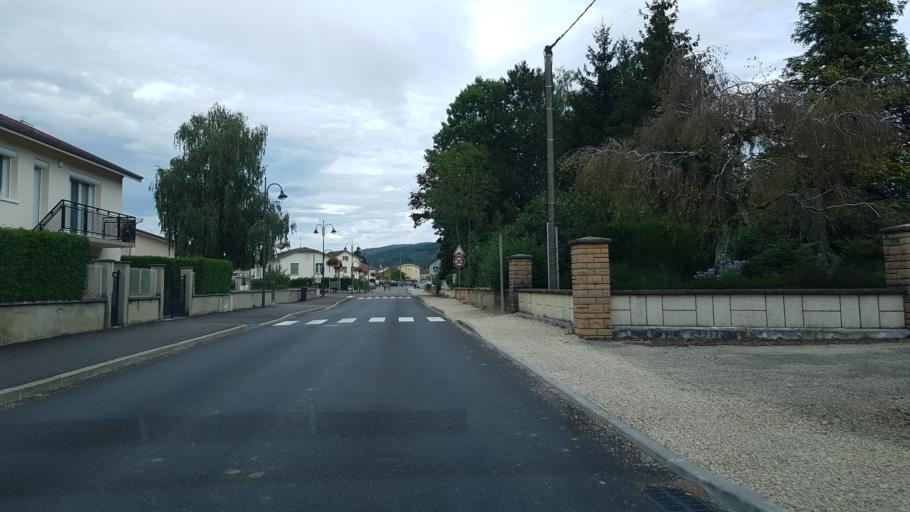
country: FR
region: Rhone-Alpes
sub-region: Departement de l'Ain
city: Villereversure
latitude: 46.1907
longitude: 5.3948
